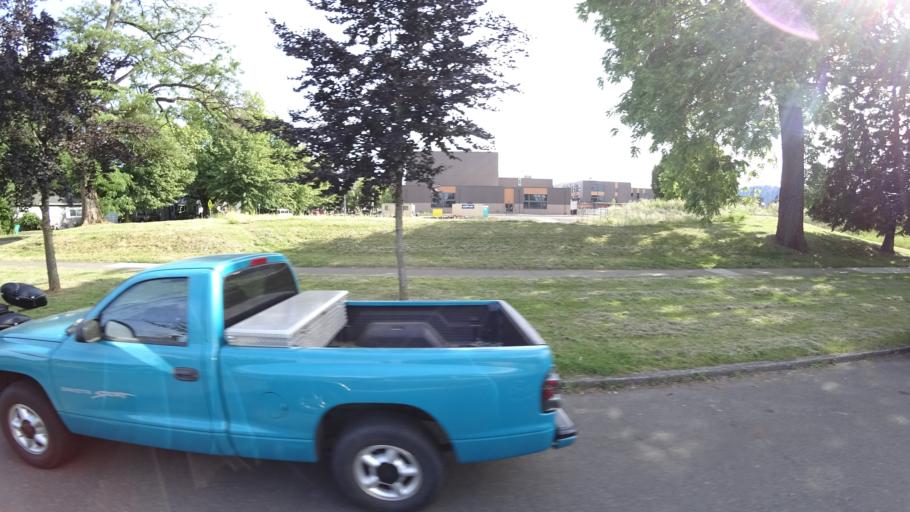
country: US
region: Oregon
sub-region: Washington County
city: West Haven
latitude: 45.5909
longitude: -122.7369
